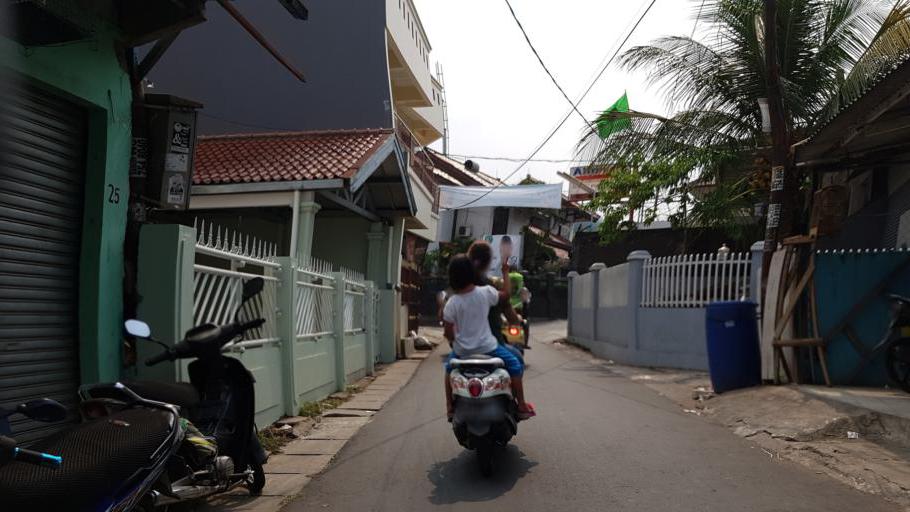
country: ID
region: West Java
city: Pamulang
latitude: -6.3295
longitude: 106.7887
